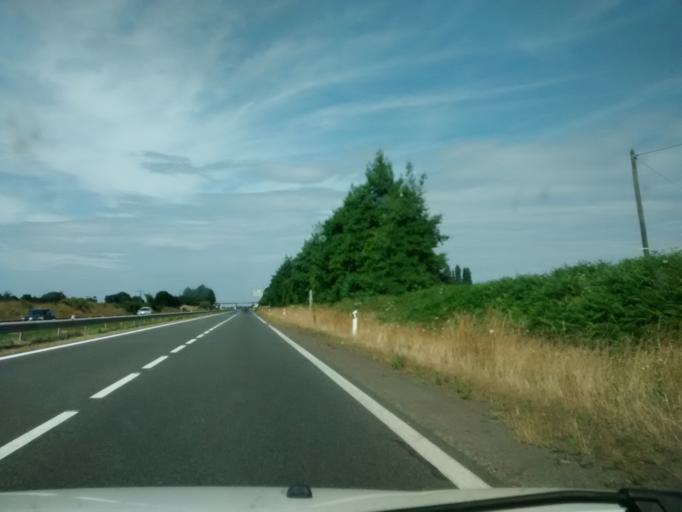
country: FR
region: Brittany
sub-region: Departement des Cotes-d'Armor
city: Tremuson
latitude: 48.5272
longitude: -2.8630
